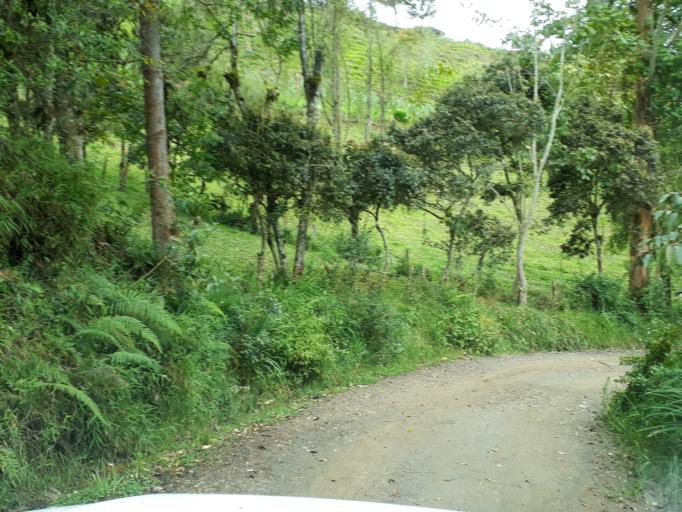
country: CO
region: Cundinamarca
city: Junin
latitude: 4.7816
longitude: -73.6479
